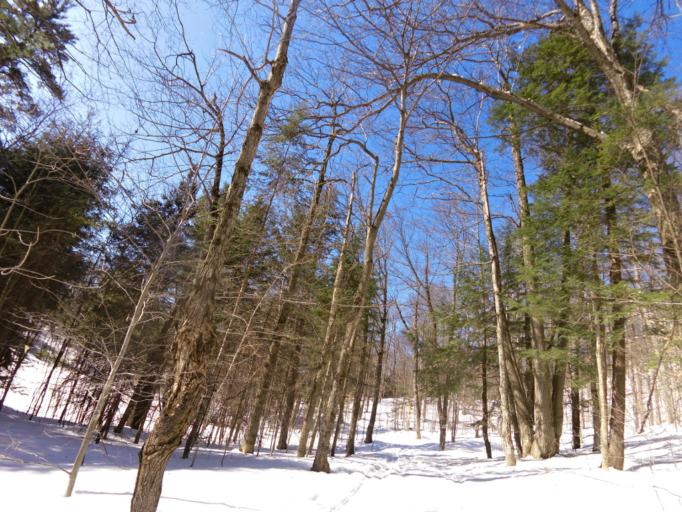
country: CA
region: Quebec
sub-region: Outaouais
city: Wakefield
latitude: 45.5088
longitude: -75.8614
